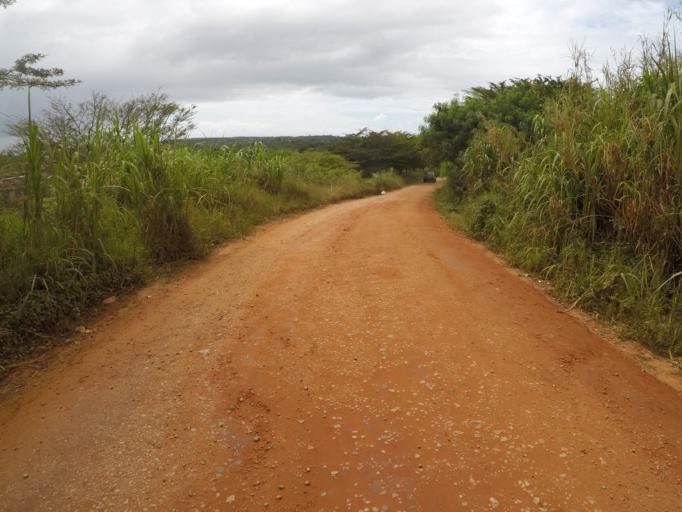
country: ZA
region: KwaZulu-Natal
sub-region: uThungulu District Municipality
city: eSikhawini
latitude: -28.8559
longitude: 31.9146
